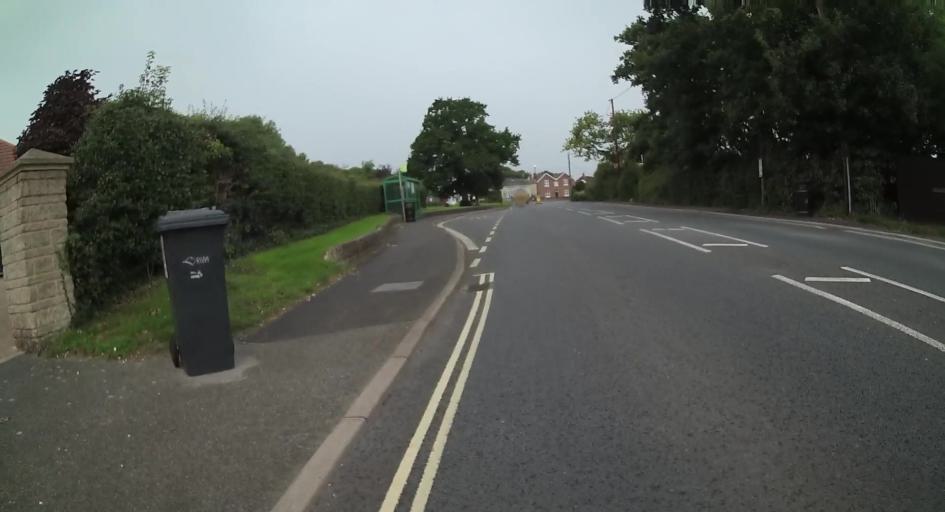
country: GB
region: England
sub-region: Isle of Wight
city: Newport
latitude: 50.6541
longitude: -1.2814
